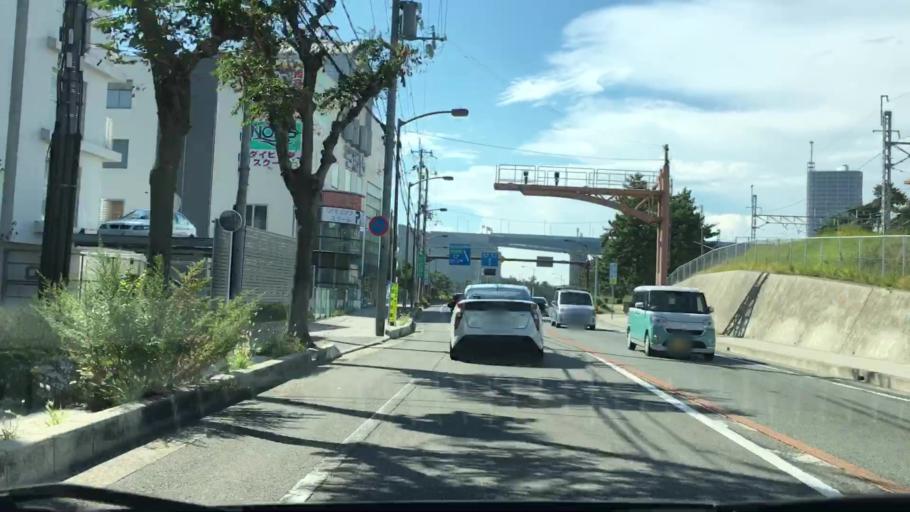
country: JP
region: Hyogo
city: Akashi
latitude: 34.6291
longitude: 135.0400
